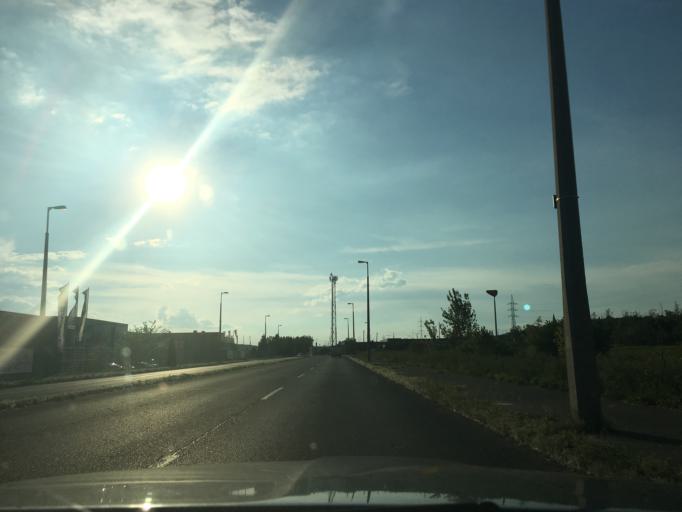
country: HU
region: Pest
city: Toeroekbalint
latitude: 47.4596
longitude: 18.8962
